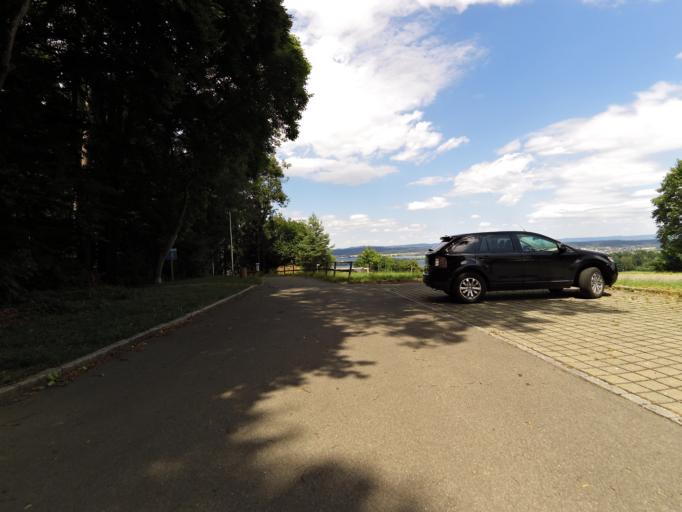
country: CH
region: Thurgau
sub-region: Kreuzlingen District
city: Ermatingen
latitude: 47.6561
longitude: 9.0804
